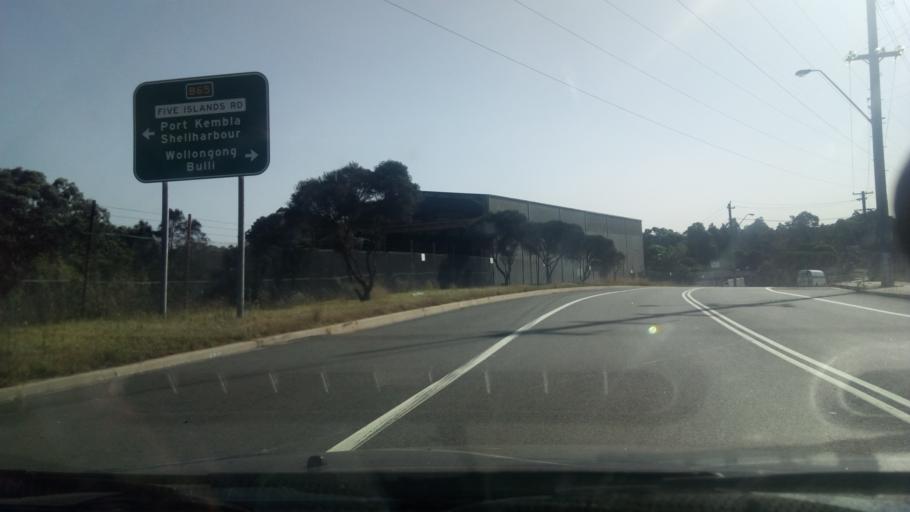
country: AU
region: New South Wales
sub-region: Wollongong
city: Cringila
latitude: -34.4729
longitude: 150.8889
